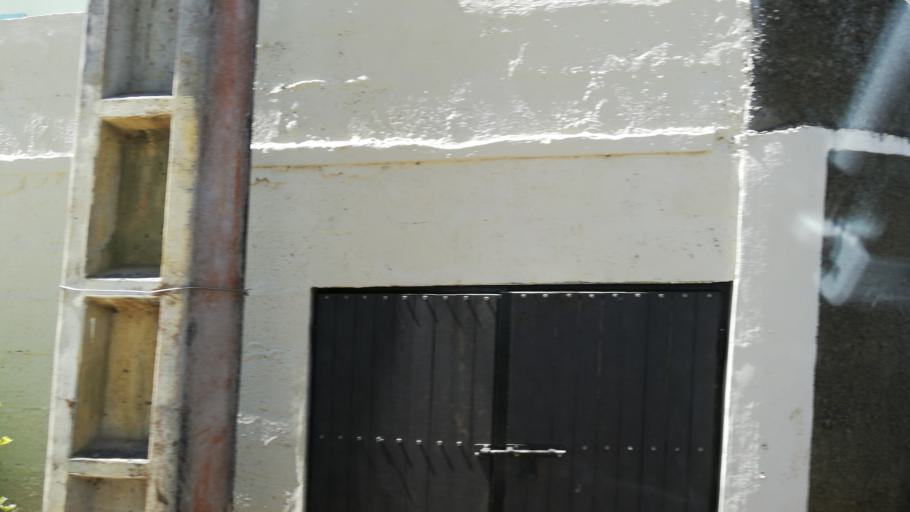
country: MU
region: Moka
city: Moka
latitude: -20.2264
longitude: 57.4705
